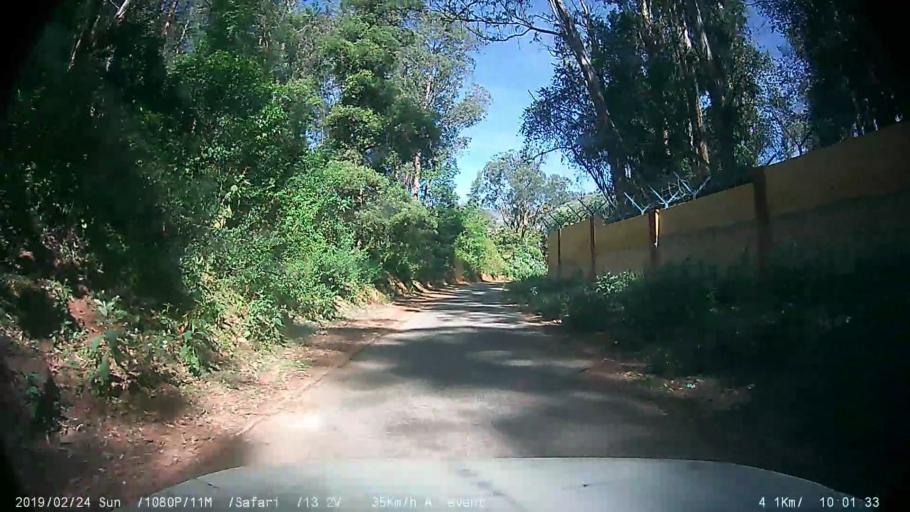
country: IN
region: Tamil Nadu
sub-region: Nilgiri
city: Aravankadu
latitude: 11.3654
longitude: 76.7566
